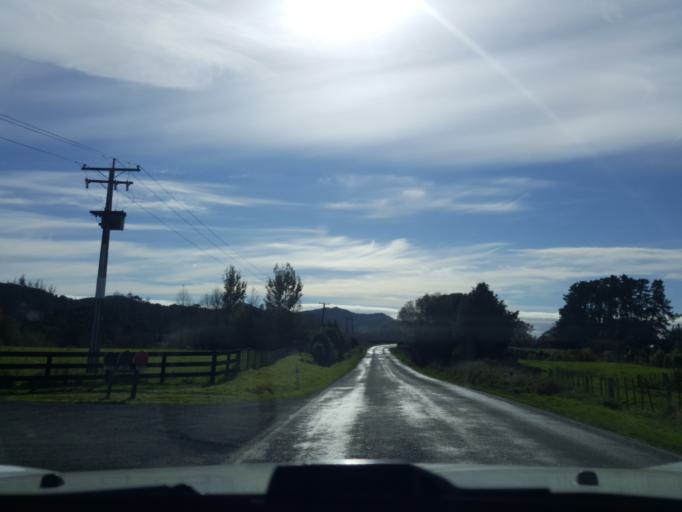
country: NZ
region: Waikato
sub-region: Waikato District
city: Ngaruawahia
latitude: -37.6078
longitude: 175.1977
